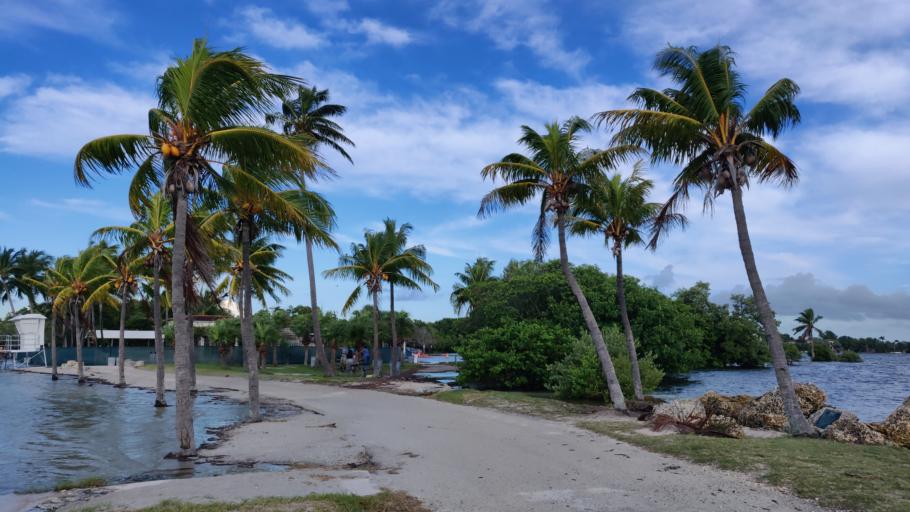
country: US
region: Florida
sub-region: Miami-Dade County
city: Coconut Grove
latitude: 25.6789
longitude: -80.2557
